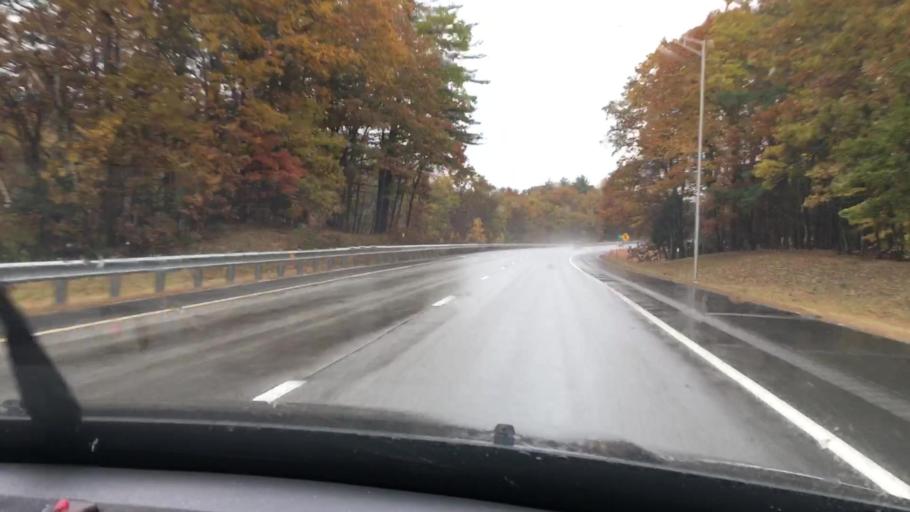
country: US
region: New Hampshire
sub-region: Merrimack County
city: Canterbury
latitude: 43.2908
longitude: -71.5723
